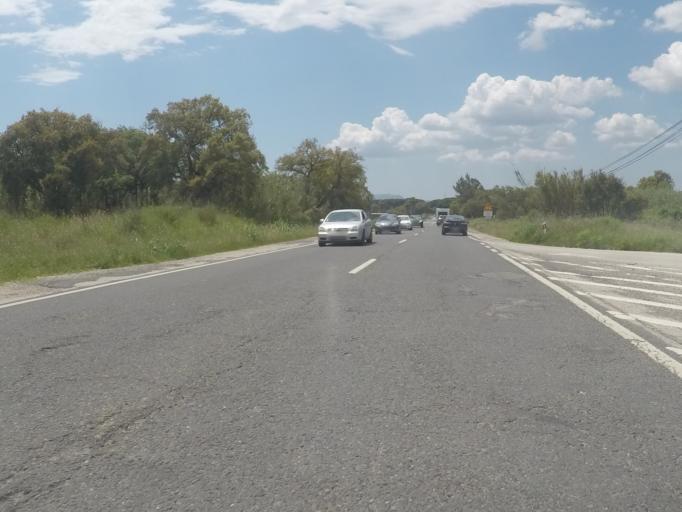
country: PT
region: Setubal
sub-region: Setubal
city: Setubal
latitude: 38.5561
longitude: -8.7996
